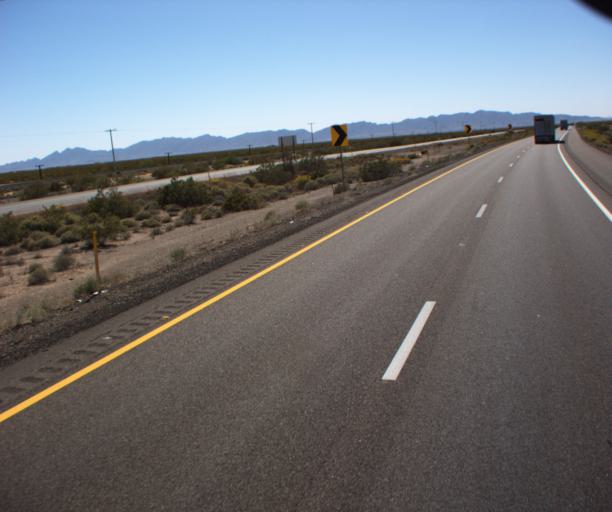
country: US
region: Arizona
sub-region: Yuma County
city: Wellton
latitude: 32.7898
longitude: -113.5596
